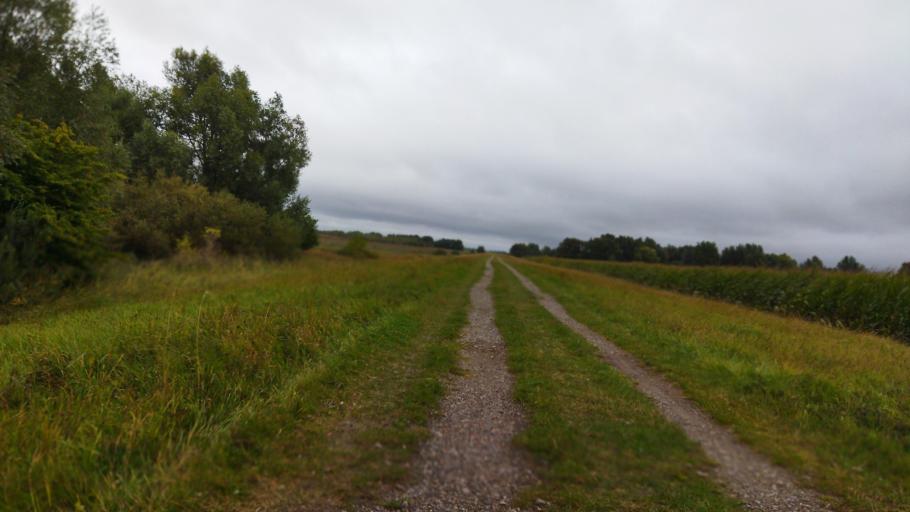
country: NL
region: Groningen
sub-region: Gemeente Delfzijl
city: Delfzijl
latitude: 53.3698
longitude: 7.0076
